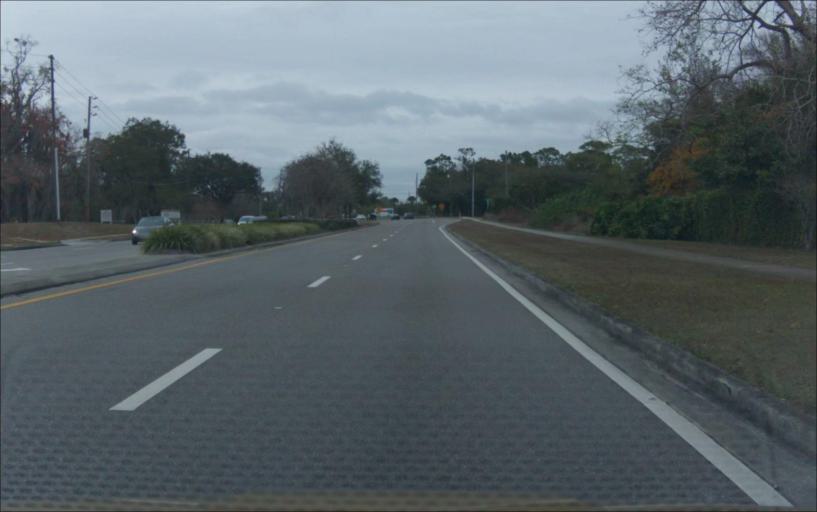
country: US
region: Florida
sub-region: Seminole County
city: Goldenrod
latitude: 28.6253
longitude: -81.3033
